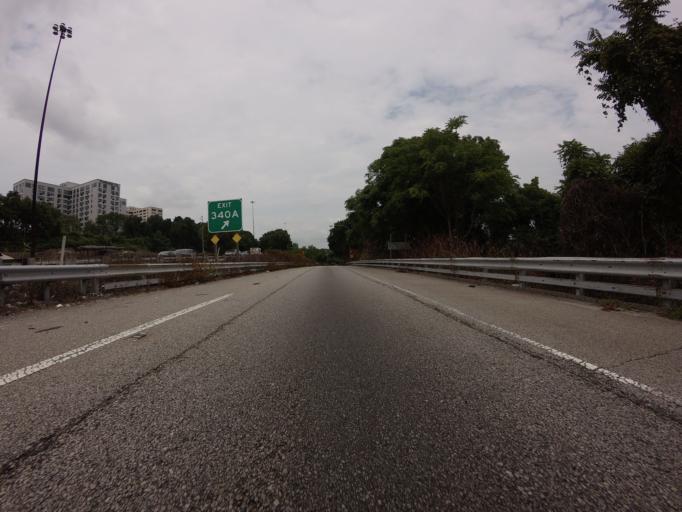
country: US
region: Pennsylvania
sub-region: Montgomery County
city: Bala-Cynwyd
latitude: 40.0088
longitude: -75.2034
